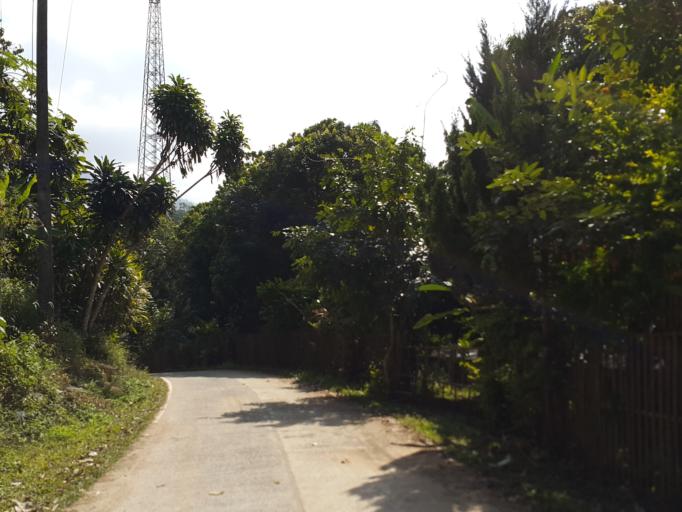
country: TH
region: Lampang
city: Wang Nuea
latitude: 19.0621
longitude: 99.3620
